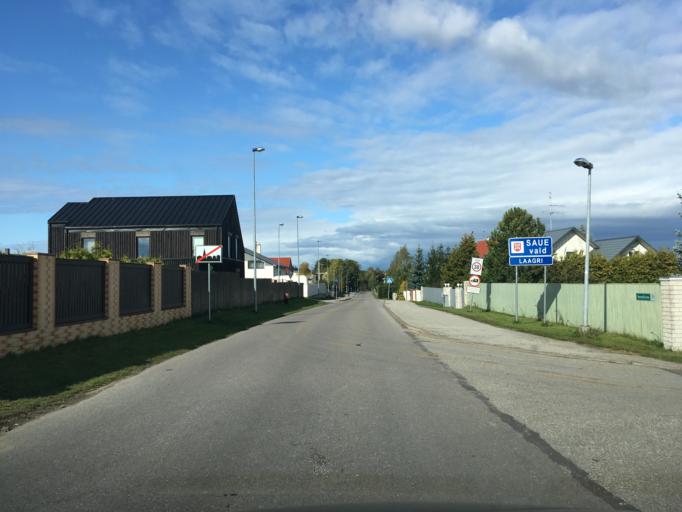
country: EE
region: Harju
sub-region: Saue vald
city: Laagri
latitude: 59.3473
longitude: 24.6410
